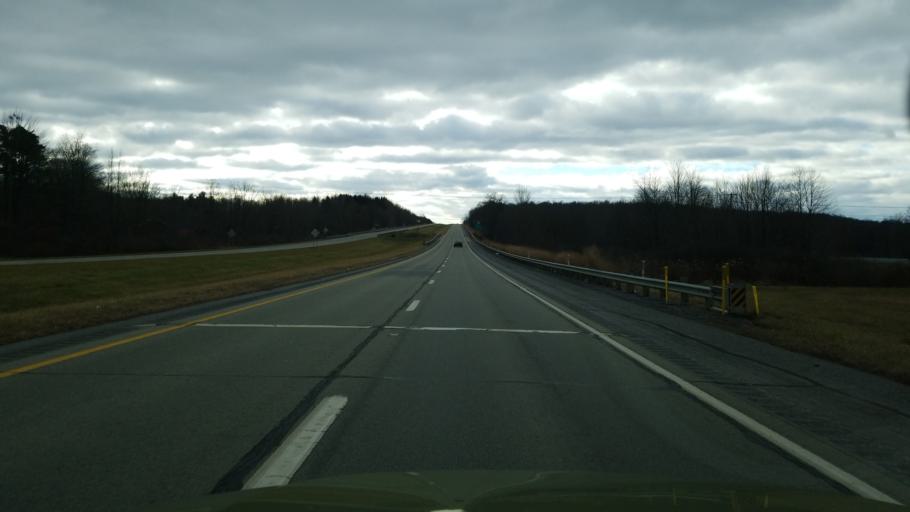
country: US
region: Pennsylvania
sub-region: Indiana County
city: Chevy Chase Heights
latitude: 40.6583
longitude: -79.1152
